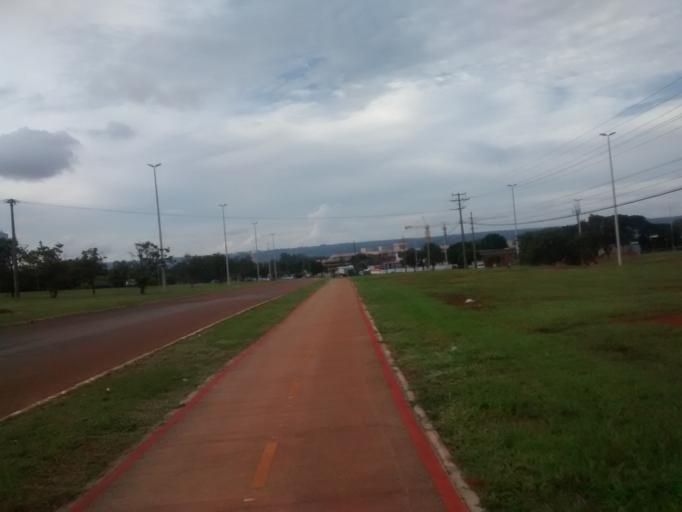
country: BR
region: Federal District
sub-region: Brasilia
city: Brasilia
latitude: -15.7925
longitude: -47.8740
